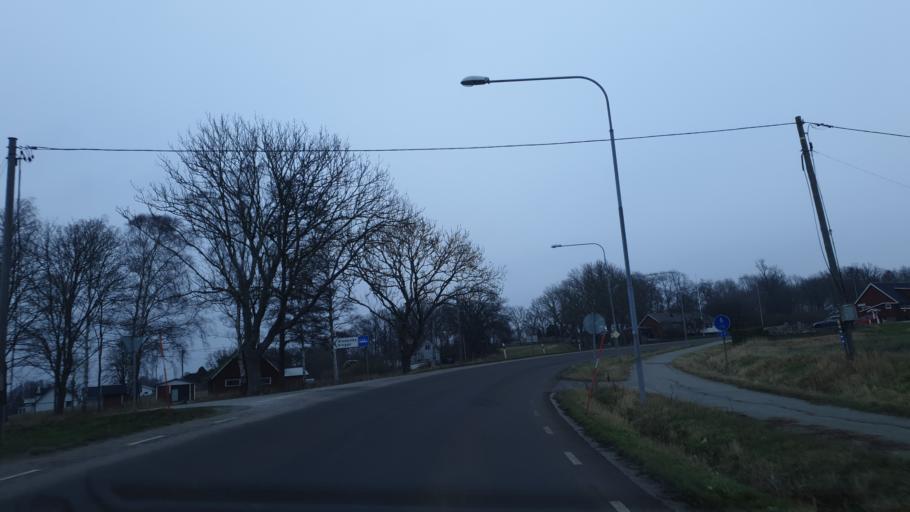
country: SE
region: Blekinge
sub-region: Karlskrona Kommun
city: Sturko
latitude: 56.1143
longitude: 15.6870
